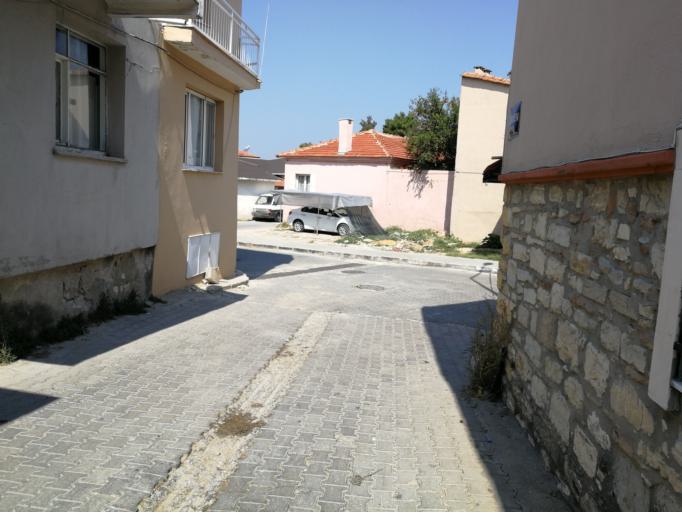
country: TR
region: Izmir
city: Urla
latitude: 38.3227
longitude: 26.7708
